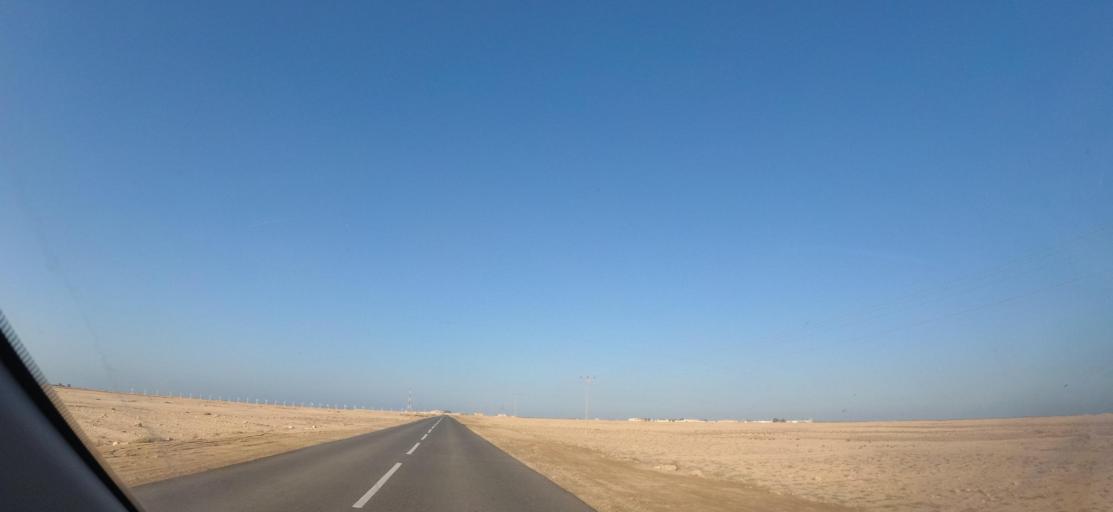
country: QA
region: Madinat ash Shamal
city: Ar Ru'ays
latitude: 26.1466
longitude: 51.2473
